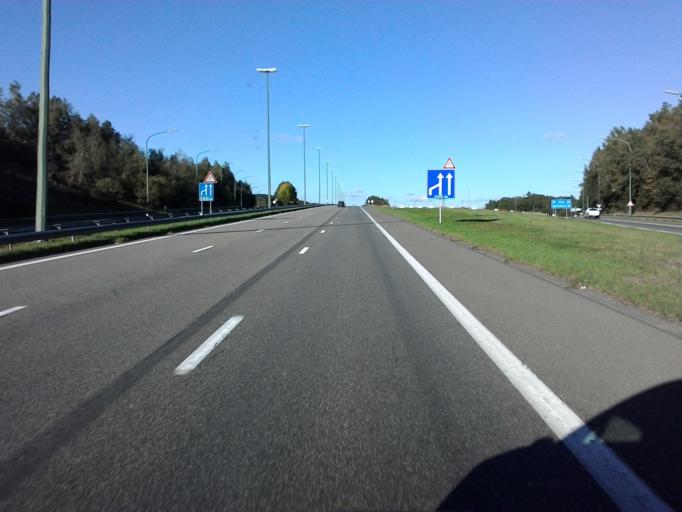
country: BE
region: Wallonia
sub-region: Province du Luxembourg
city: Houffalize
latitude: 50.1415
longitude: 5.7810
